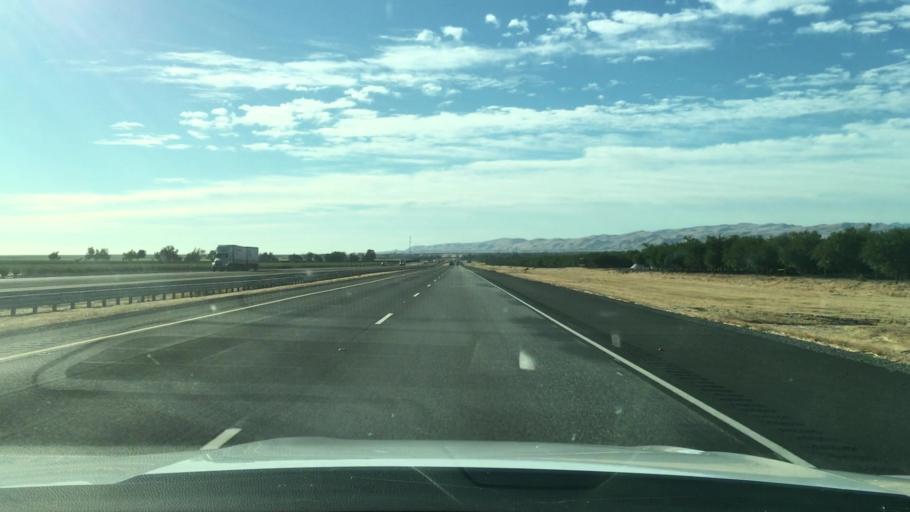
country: US
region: California
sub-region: Fresno County
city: Firebaugh
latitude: 36.6631
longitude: -120.6412
